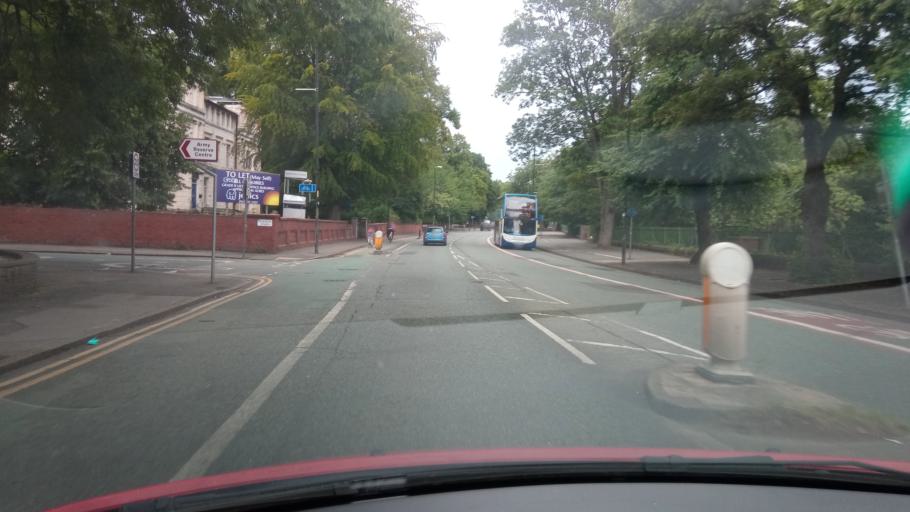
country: GB
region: England
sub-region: Manchester
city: Fallowfield
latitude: 53.4501
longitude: -2.2209
